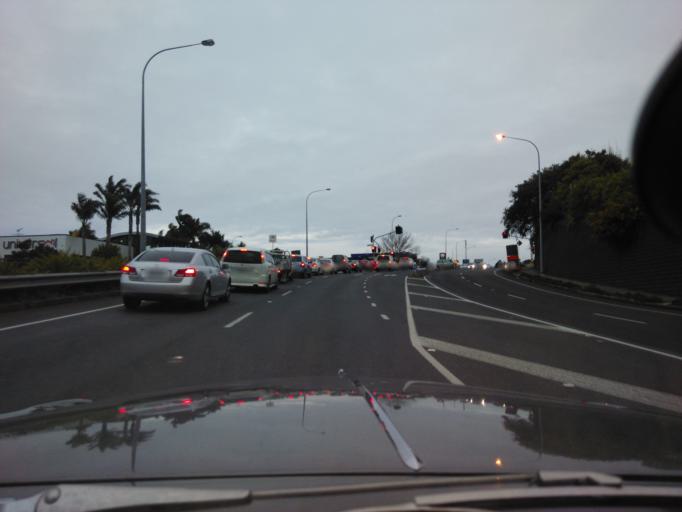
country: NZ
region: Auckland
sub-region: Auckland
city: Rothesay Bay
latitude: -36.7552
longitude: 174.7005
